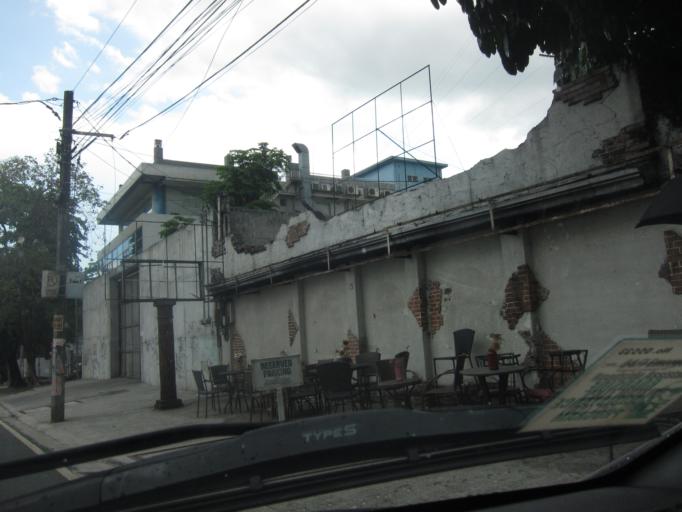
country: PH
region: Metro Manila
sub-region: Quezon City
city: Quezon City
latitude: 14.6368
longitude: 121.0547
